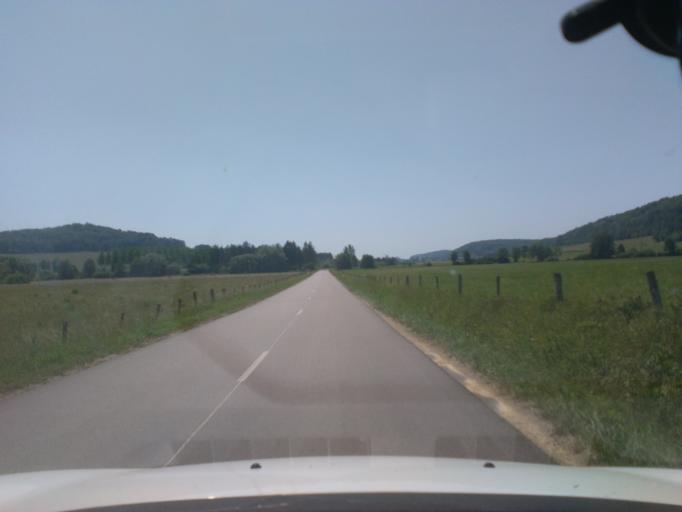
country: FR
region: Lorraine
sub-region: Departement des Vosges
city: Liffol-le-Grand
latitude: 48.3825
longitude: 5.6246
